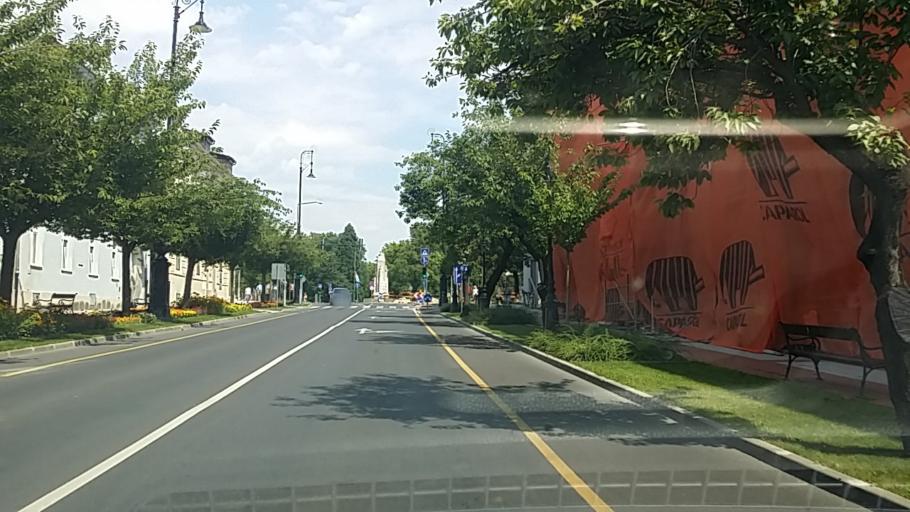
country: HU
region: Zala
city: Nagykanizsa
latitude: 46.4552
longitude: 16.9944
